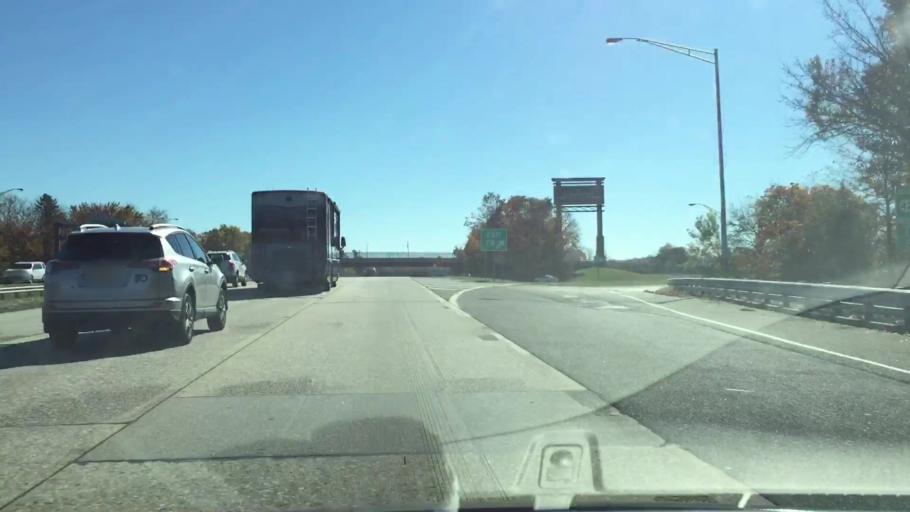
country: US
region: New Jersey
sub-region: Gloucester County
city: Turnersville
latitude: 39.7891
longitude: -75.0493
